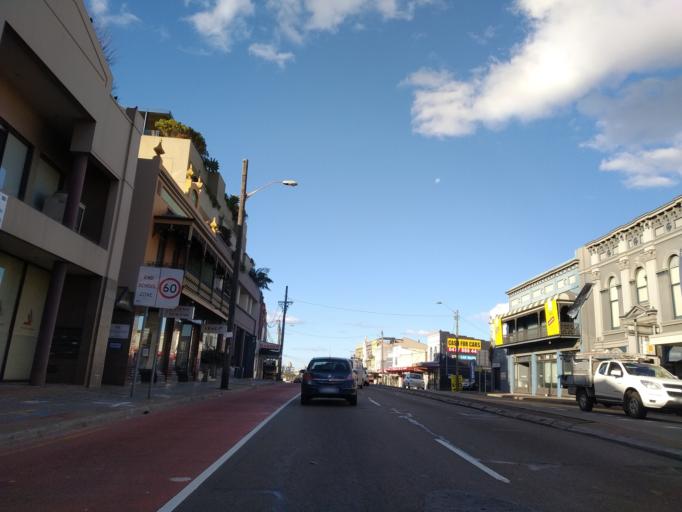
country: AU
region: New South Wales
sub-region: Marrickville
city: Lewisham
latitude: -33.8888
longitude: 151.1544
